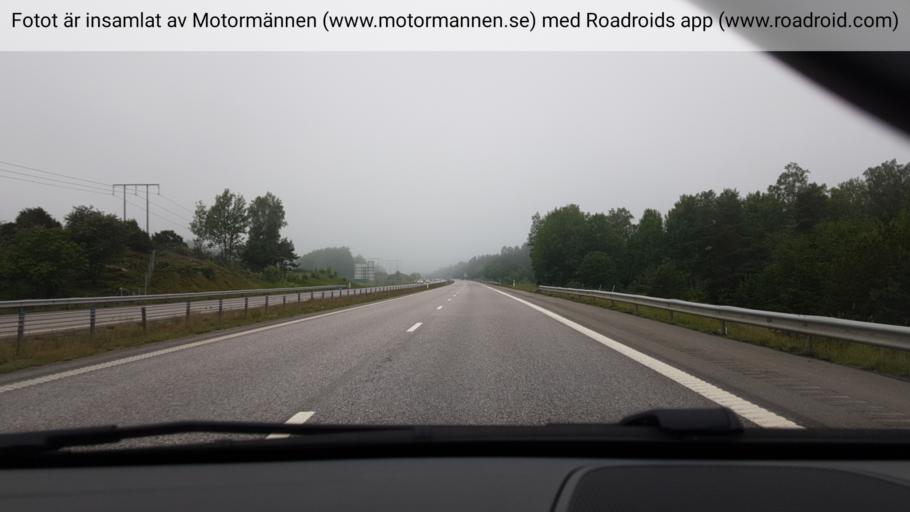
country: SE
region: OEstergoetland
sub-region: Norrkopings Kommun
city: Kimstad
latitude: 58.4875
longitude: 15.9249
